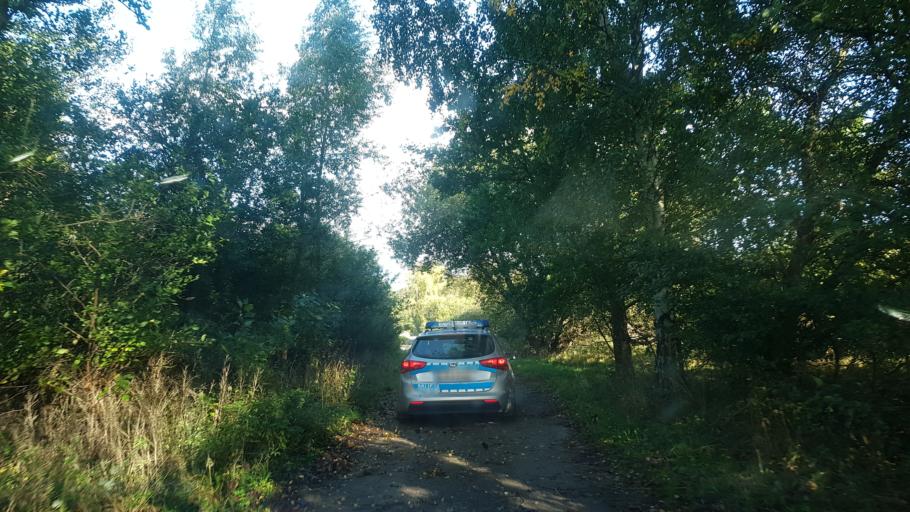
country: PL
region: West Pomeranian Voivodeship
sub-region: Powiat kolobrzeski
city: Grzybowo
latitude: 54.1676
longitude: 15.5158
